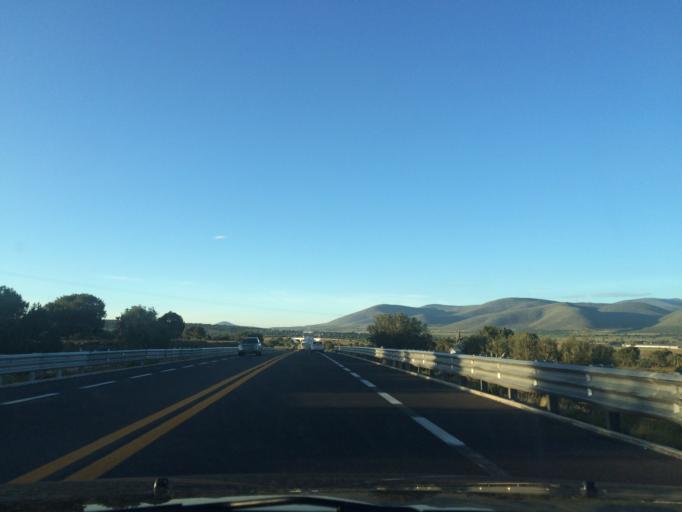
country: MX
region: Puebla
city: Cuacnopalan
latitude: 18.7803
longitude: -97.4874
